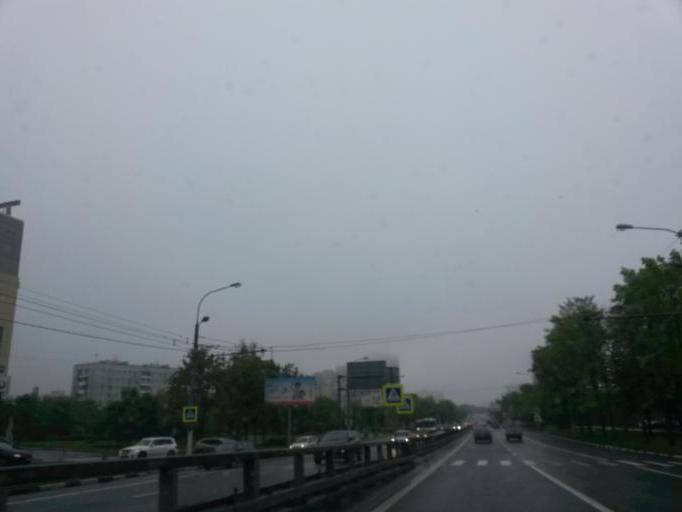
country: RU
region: Moscow
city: Yasenevo
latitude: 55.6363
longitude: 37.5219
